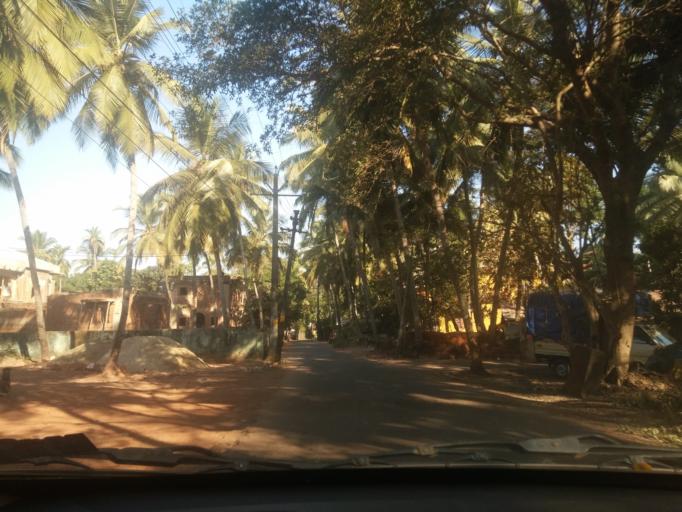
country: IN
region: Goa
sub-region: South Goa
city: Colva
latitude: 15.3087
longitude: 73.9118
